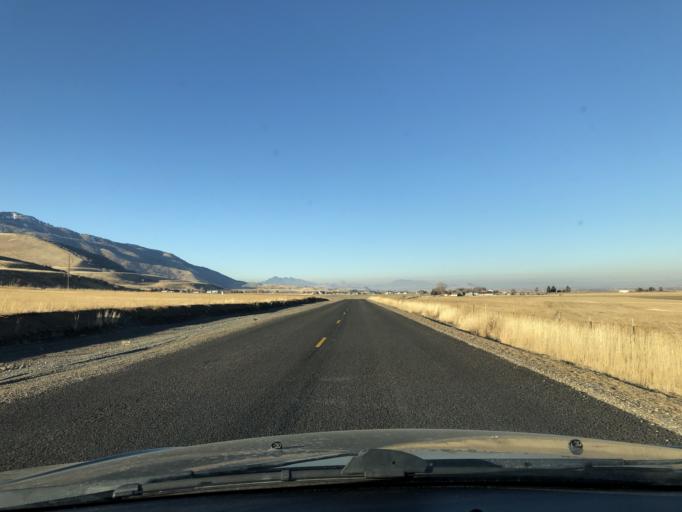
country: US
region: Utah
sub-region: Cache County
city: Wellsville
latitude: 41.5953
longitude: -111.9277
